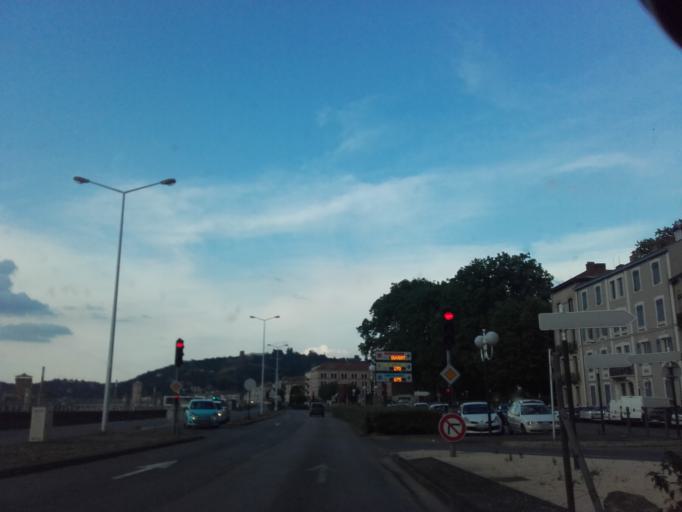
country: FR
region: Rhone-Alpes
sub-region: Departement de l'Isere
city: Vienne
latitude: 45.5207
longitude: 4.8678
